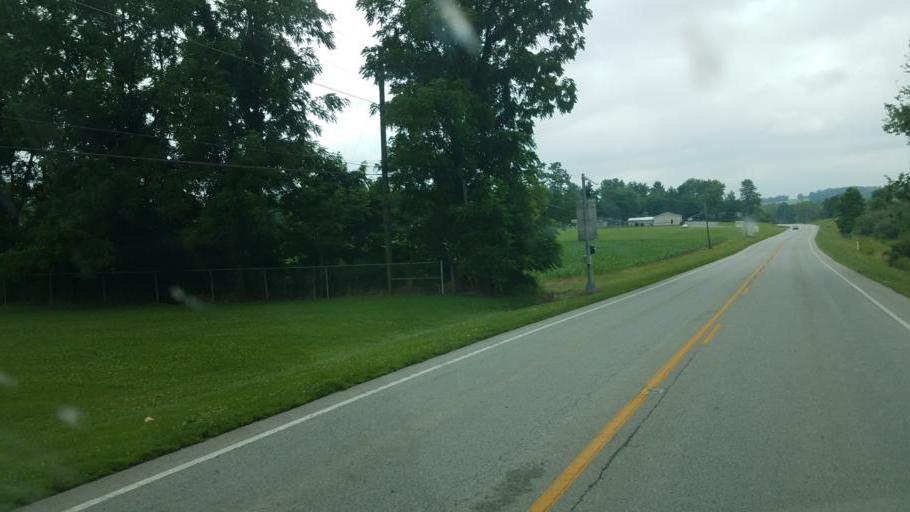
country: US
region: Ohio
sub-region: Highland County
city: Hillsboro
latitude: 39.2107
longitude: -83.5604
